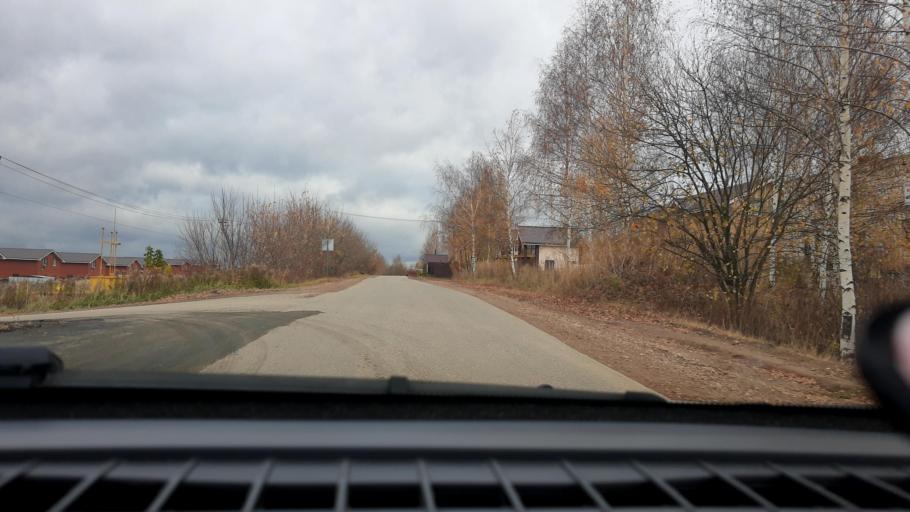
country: RU
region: Nizjnij Novgorod
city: Afonino
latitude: 56.2033
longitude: 44.1384
